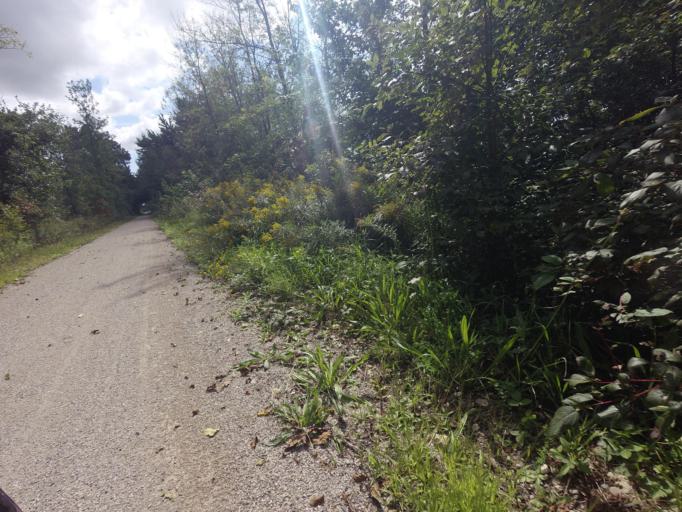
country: CA
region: Ontario
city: Huron East
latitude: 43.6176
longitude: -81.1479
